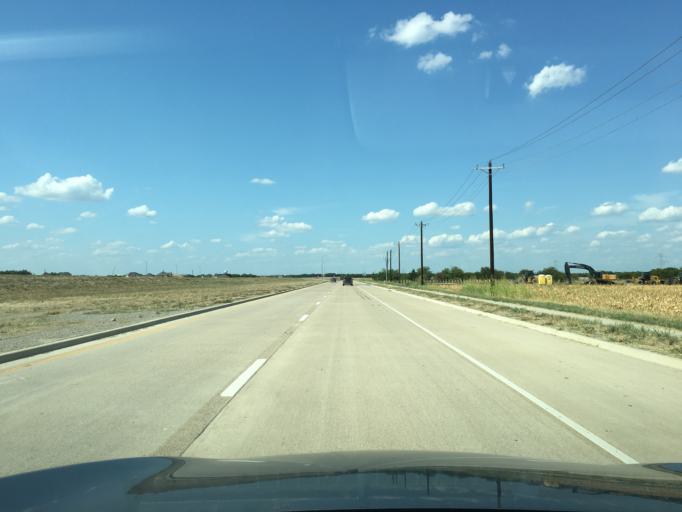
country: US
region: Texas
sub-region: Tarrant County
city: Mansfield
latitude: 32.5284
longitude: -97.0815
